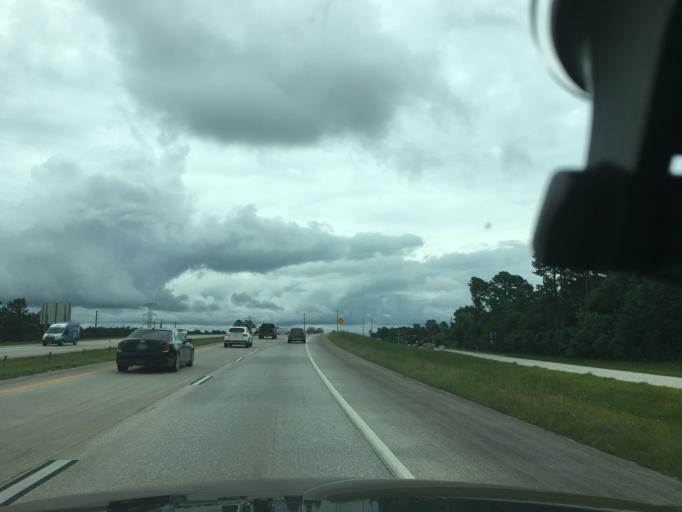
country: US
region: Texas
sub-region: Montgomery County
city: The Woodlands
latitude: 30.0943
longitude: -95.5100
